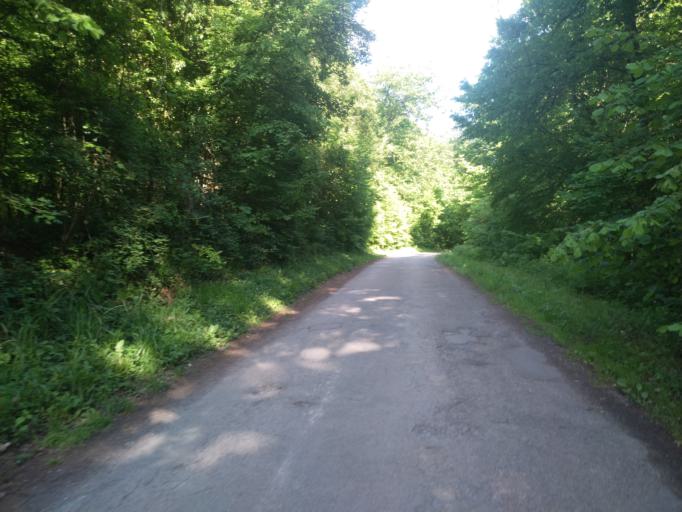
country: DE
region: Baden-Wuerttemberg
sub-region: Karlsruhe Region
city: Ostringen
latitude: 49.1680
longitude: 8.7084
